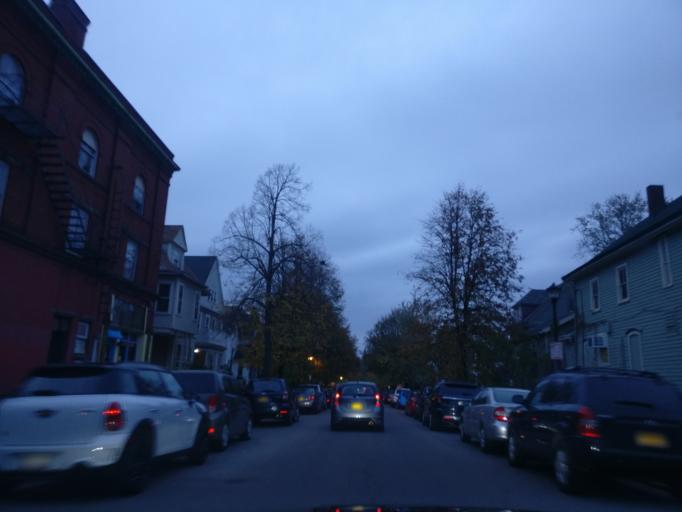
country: US
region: New York
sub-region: Erie County
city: Buffalo
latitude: 42.9132
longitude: -78.8787
